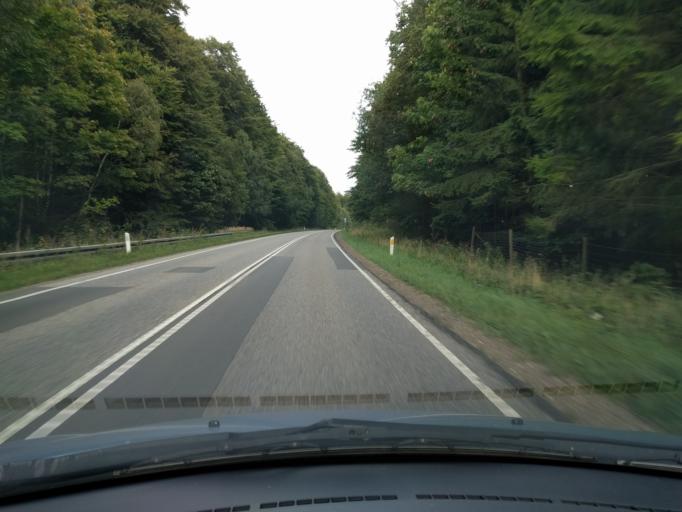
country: DK
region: Zealand
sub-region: Vordingborg Kommune
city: Nyrad
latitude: 55.0206
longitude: 11.9419
